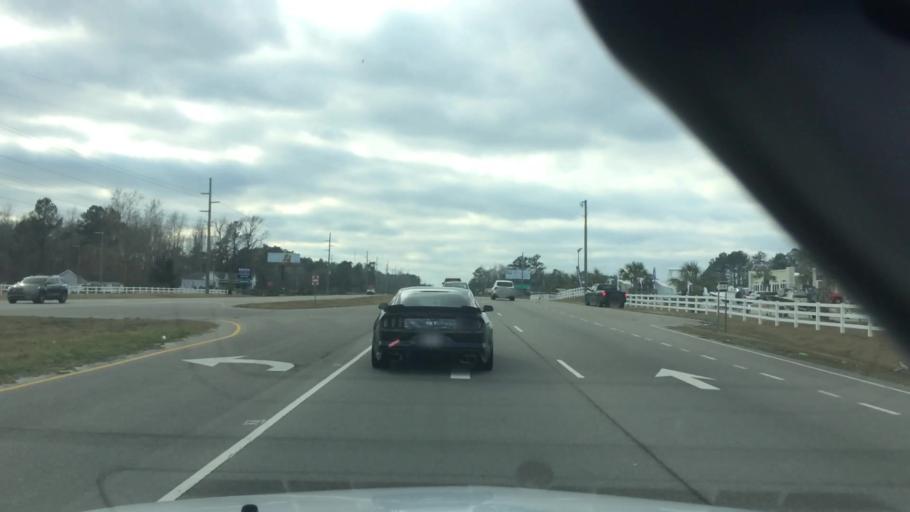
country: US
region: North Carolina
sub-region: Brunswick County
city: Shallotte
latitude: 34.0090
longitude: -78.2970
